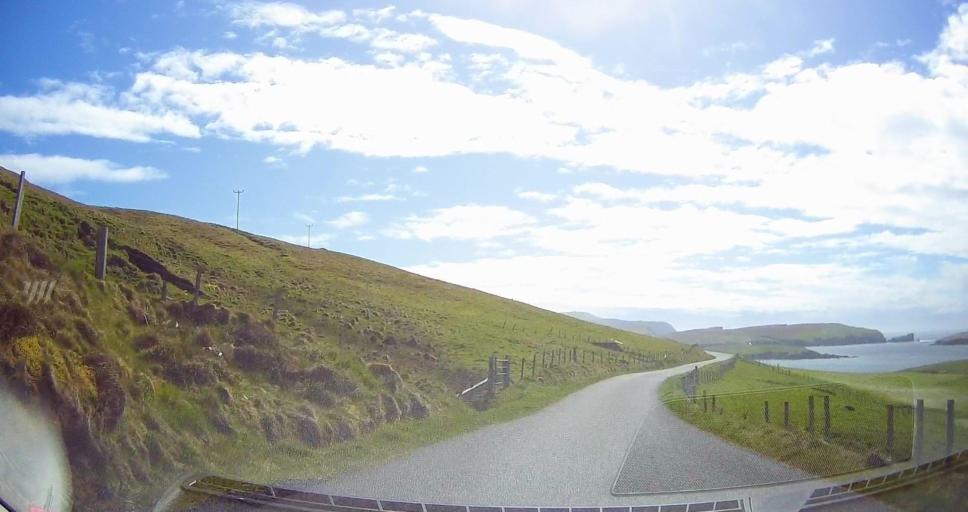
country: GB
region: Scotland
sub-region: Shetland Islands
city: Sandwick
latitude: 59.9555
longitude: -1.3257
